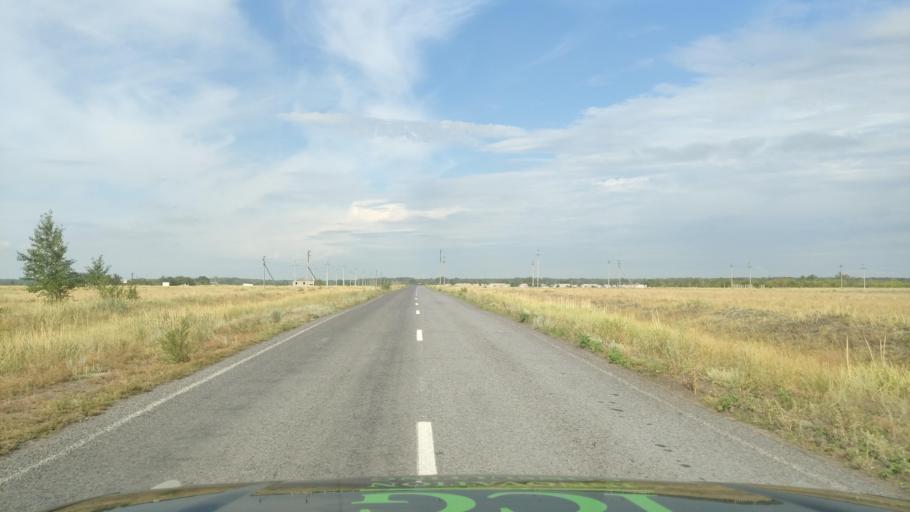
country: KZ
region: Pavlodar
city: Leninskiy
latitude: 52.4778
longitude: 76.8339
